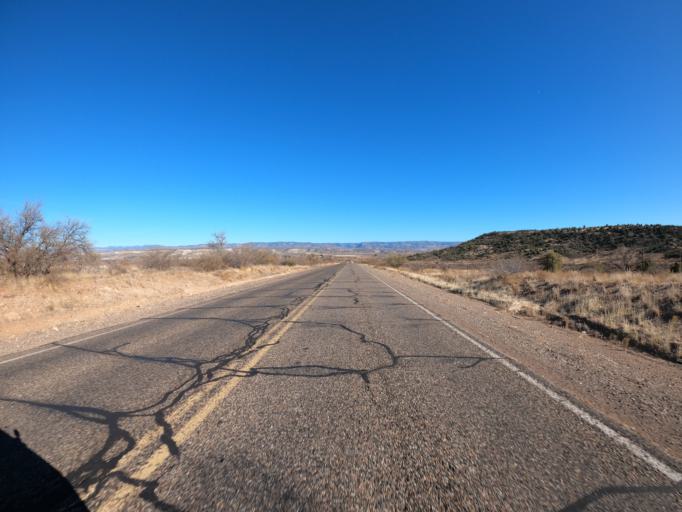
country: US
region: Arizona
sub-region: Yavapai County
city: Camp Verde
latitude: 34.5577
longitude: -111.8886
